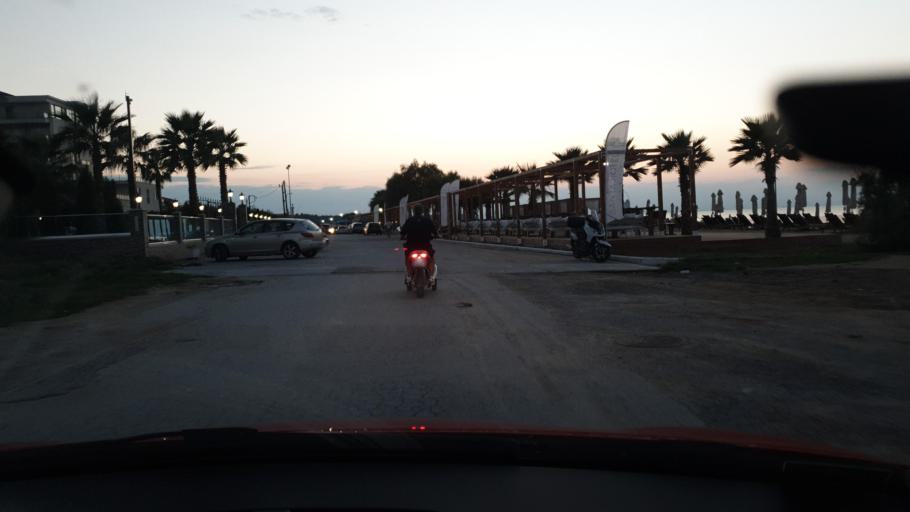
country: GR
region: Central Macedonia
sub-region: Nomos Thessalonikis
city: Neoi Epivates
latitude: 40.5028
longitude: 22.8972
